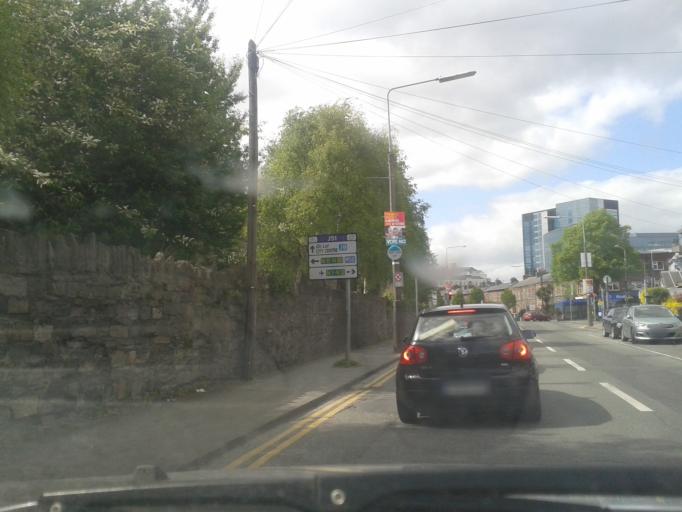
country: IE
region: Leinster
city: Ringsend
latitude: 53.3365
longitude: -6.2337
